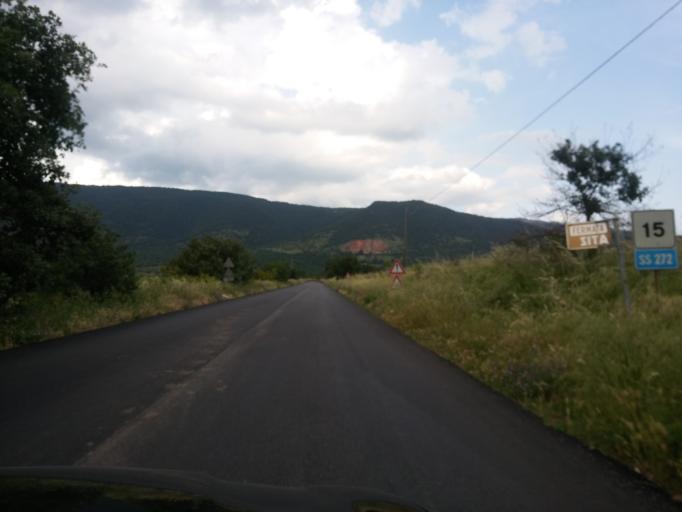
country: IT
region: Apulia
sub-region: Provincia di Foggia
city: Rignano Garganico
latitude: 41.7167
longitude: 15.5592
